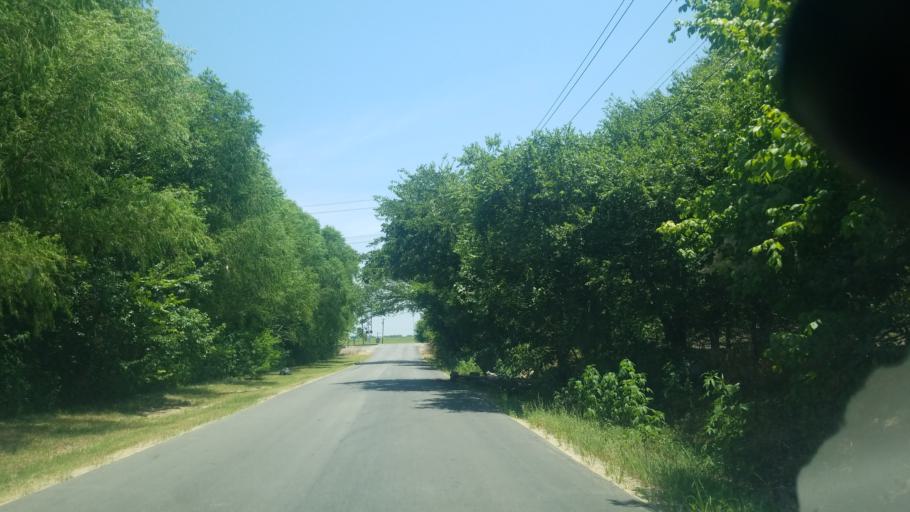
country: US
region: Texas
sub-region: Dallas County
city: Dallas
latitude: 32.7323
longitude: -96.7794
